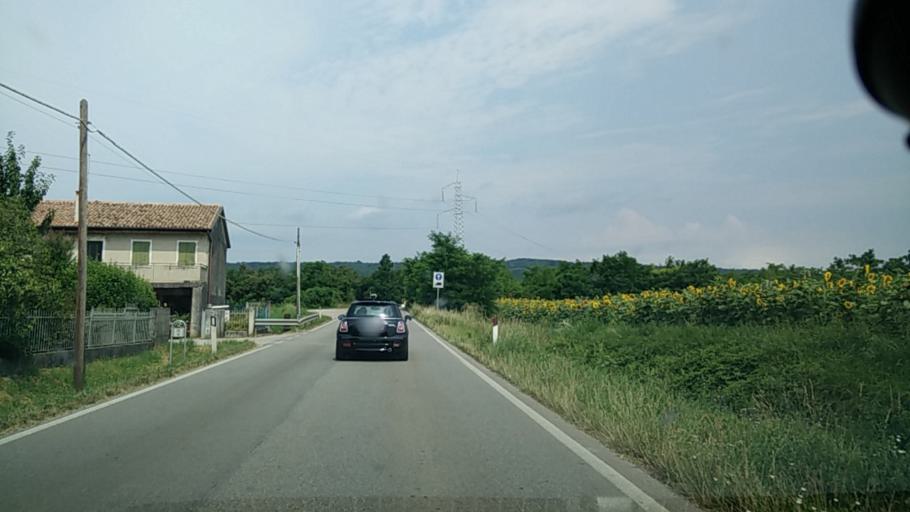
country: IT
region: Veneto
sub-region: Provincia di Treviso
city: Selva del Montello
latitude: 45.7757
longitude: 12.1398
